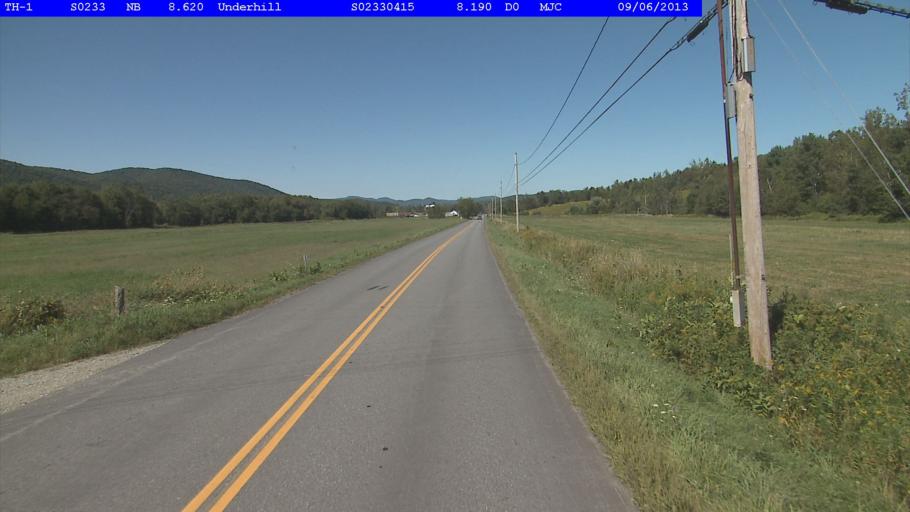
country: US
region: Vermont
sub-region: Chittenden County
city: Jericho
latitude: 44.5826
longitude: -72.8634
